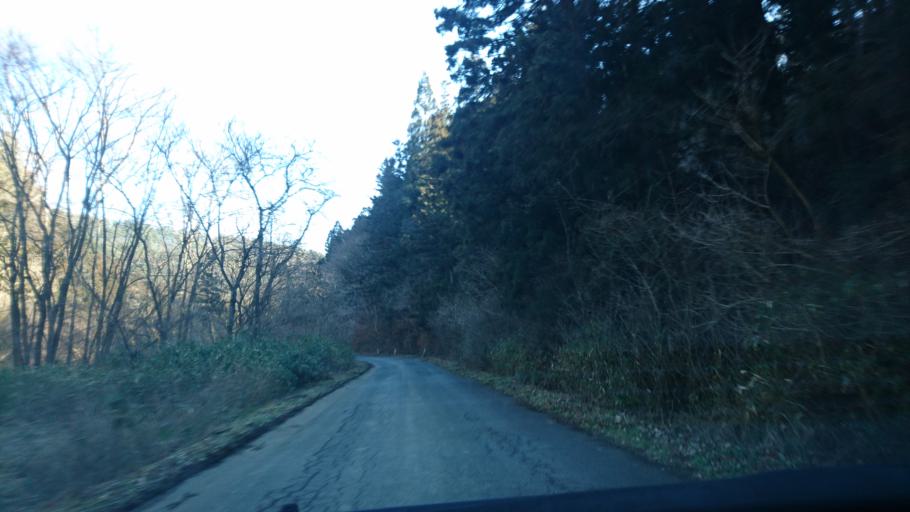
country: JP
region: Iwate
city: Ichinoseki
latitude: 38.7954
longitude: 141.2580
